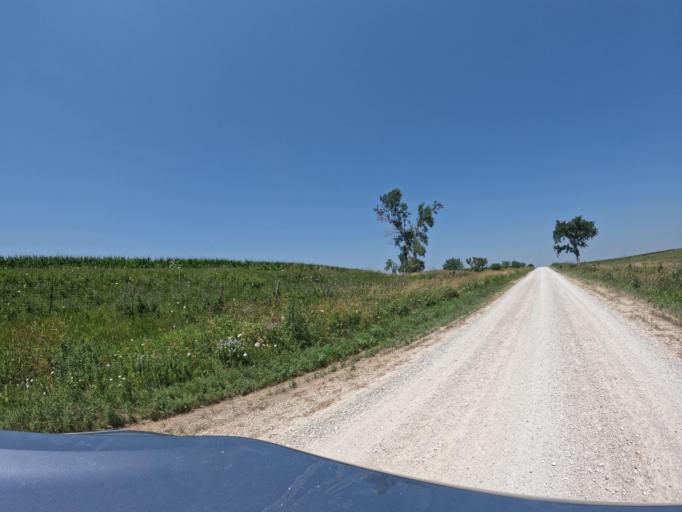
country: US
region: Iowa
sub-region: Keokuk County
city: Sigourney
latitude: 41.2658
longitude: -92.1803
